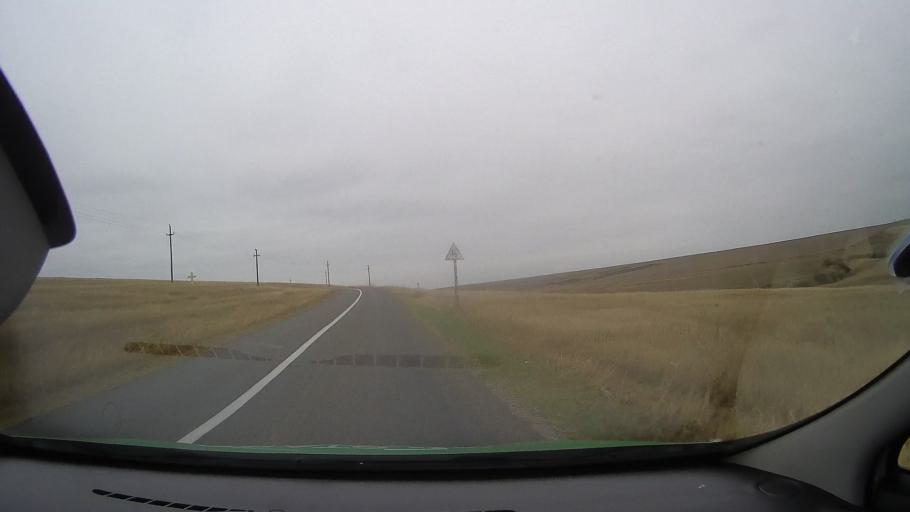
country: RO
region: Constanta
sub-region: Comuna Saraiu
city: Saraiu
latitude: 44.7271
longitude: 28.2116
